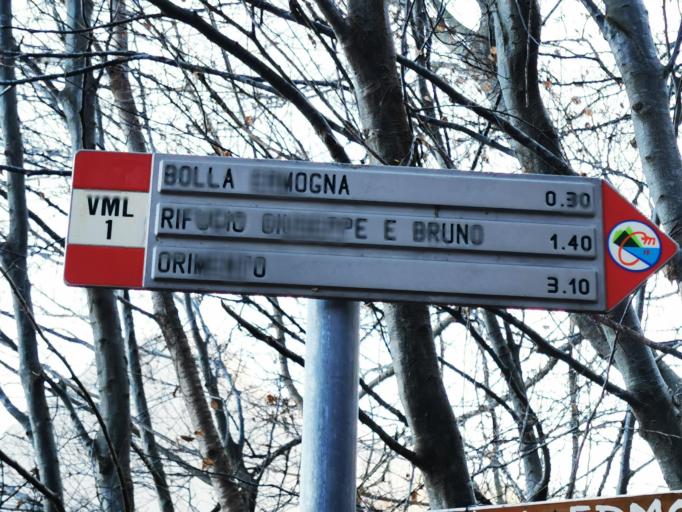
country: IT
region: Lombardy
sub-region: Provincia di Como
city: Casasco Intelvi
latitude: 45.9232
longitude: 9.0717
